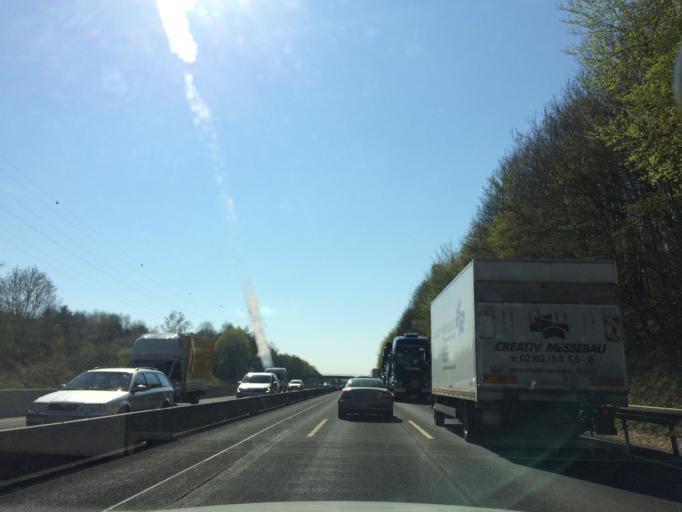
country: DE
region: North Rhine-Westphalia
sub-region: Regierungsbezirk Dusseldorf
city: Erkrath
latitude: 51.2153
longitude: 6.9249
